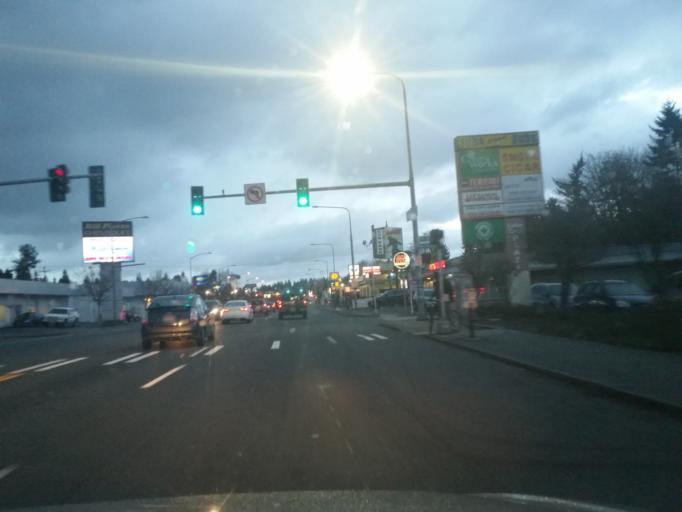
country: US
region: Washington
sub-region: King County
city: Lake Forest Park
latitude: 47.7100
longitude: -122.3006
